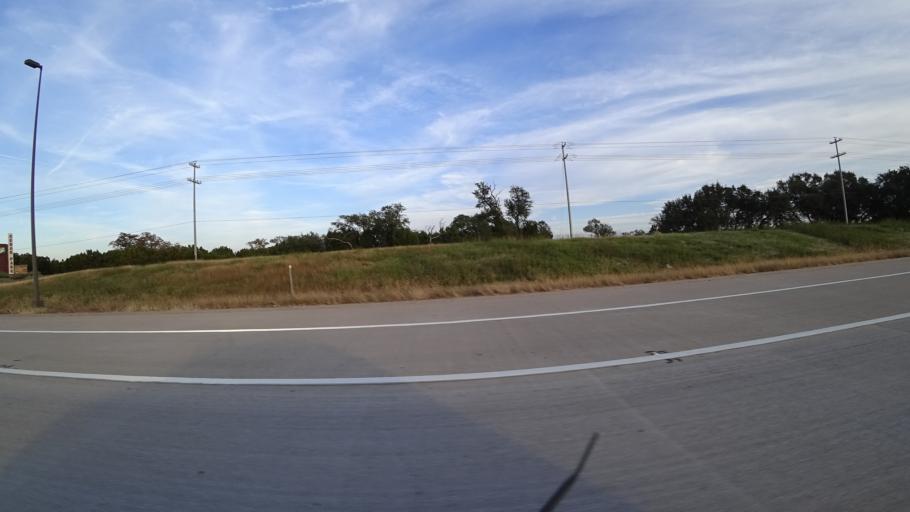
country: US
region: Texas
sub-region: Williamson County
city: Cedar Park
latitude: 30.4932
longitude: -97.8023
